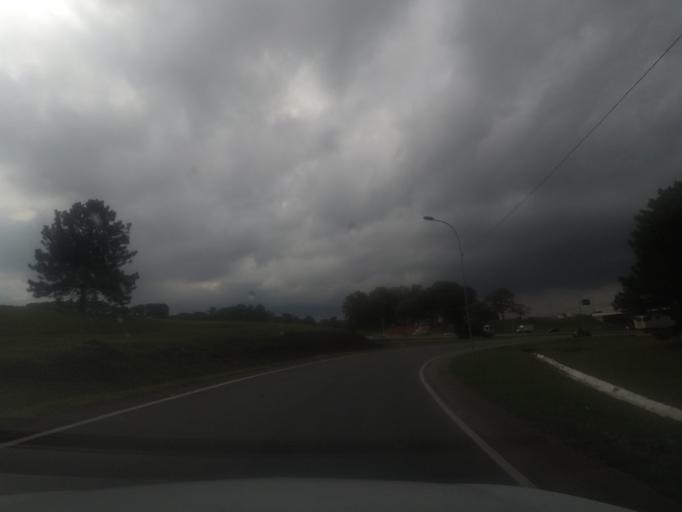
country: BR
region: Parana
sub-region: Sao Jose Dos Pinhais
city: Sao Jose dos Pinhais
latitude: -25.5449
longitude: -49.3052
